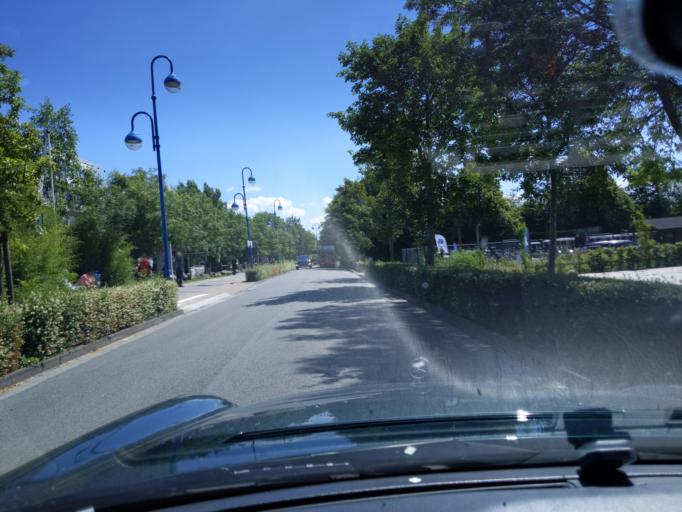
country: DE
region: Lower Saxony
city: Butjadingen
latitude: 53.5761
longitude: 8.2503
